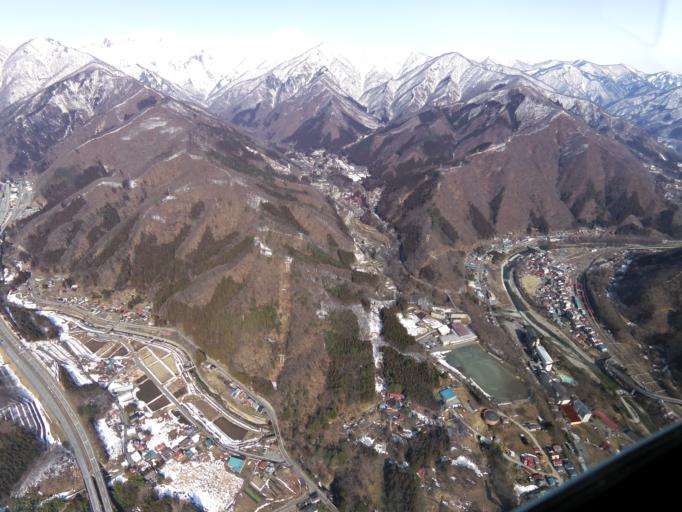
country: JP
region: Gunma
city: Numata
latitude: 36.7699
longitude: 138.9636
